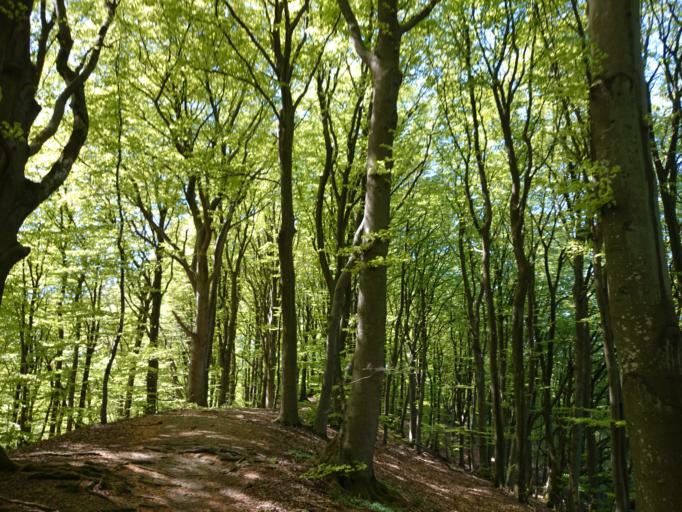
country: SE
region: Skane
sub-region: Lunds Kommun
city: Genarp
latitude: 55.6722
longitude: 13.4074
